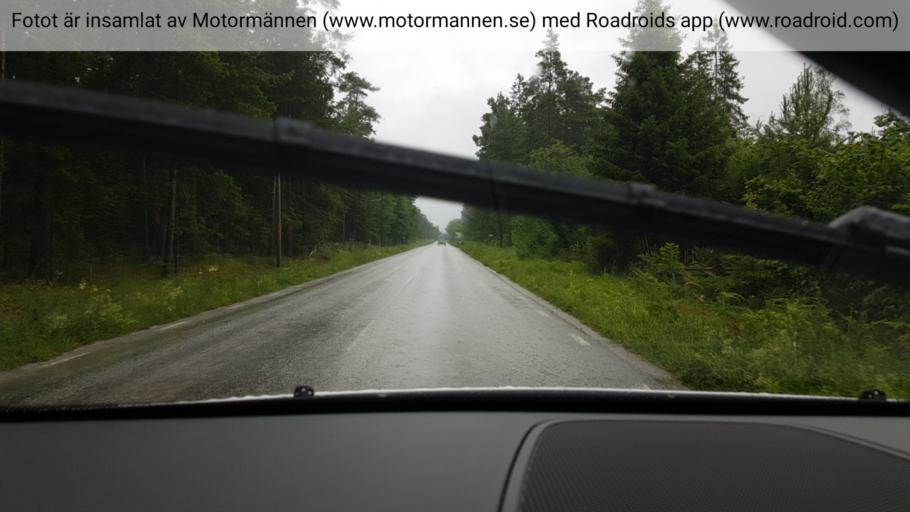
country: SE
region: Gotland
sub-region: Gotland
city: Slite
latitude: 57.6223
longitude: 18.7594
